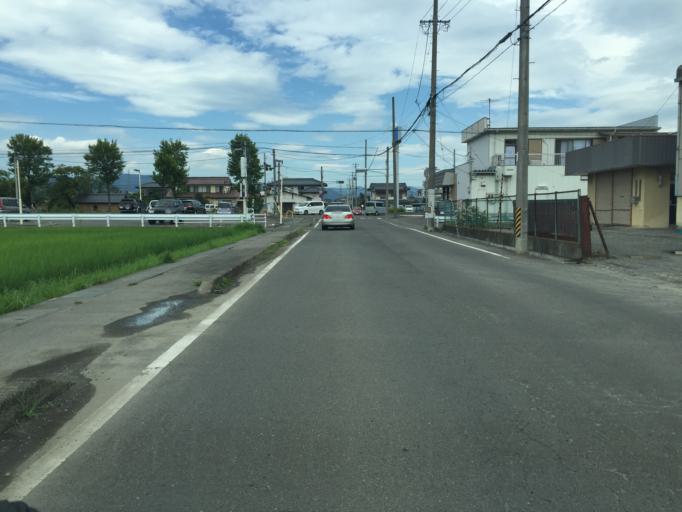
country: JP
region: Fukushima
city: Fukushima-shi
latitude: 37.7382
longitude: 140.4179
